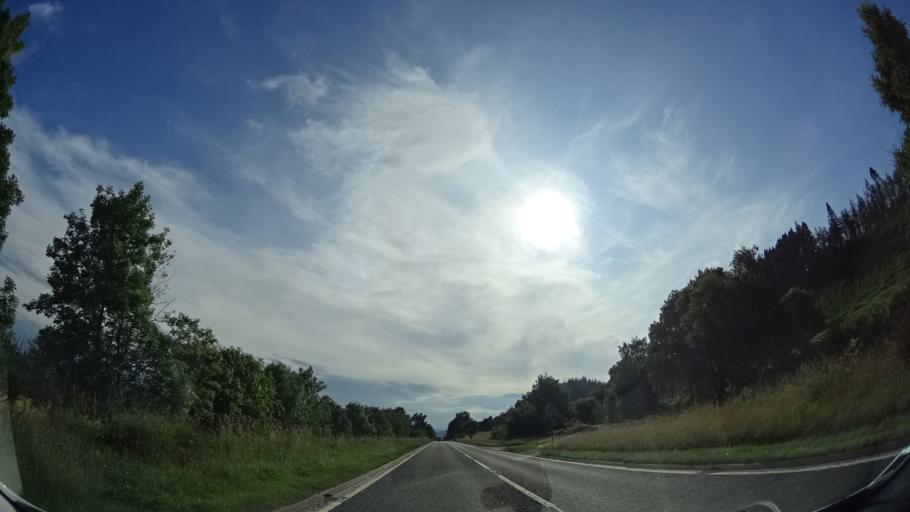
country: GB
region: Scotland
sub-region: Highland
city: Conon Bridge
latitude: 57.5639
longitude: -4.4838
